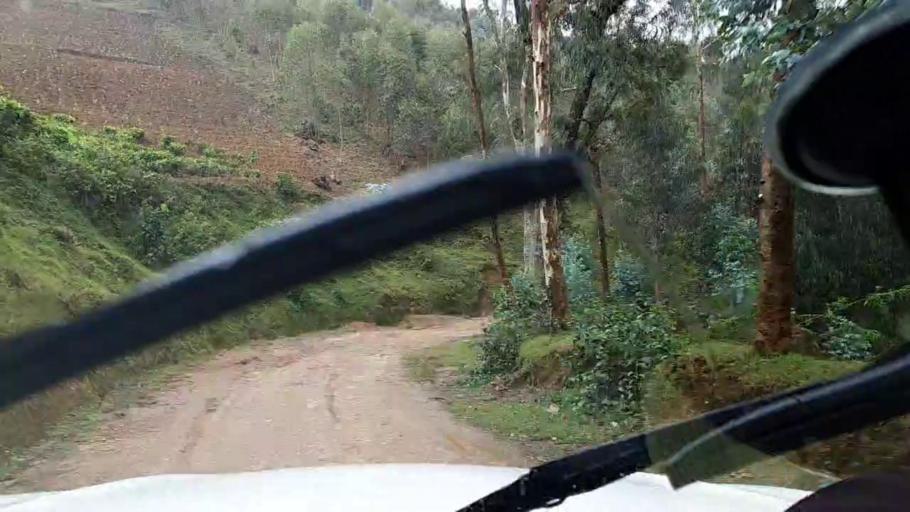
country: RW
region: Western Province
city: Kibuye
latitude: -2.0757
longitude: 29.5125
